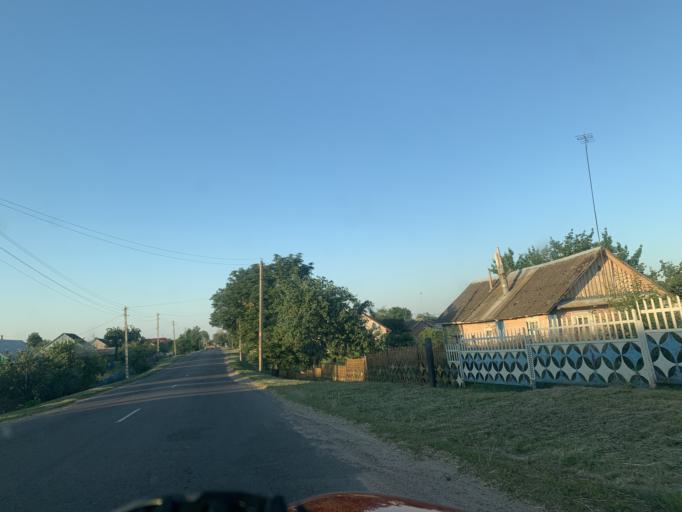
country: BY
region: Minsk
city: Haradzyeya
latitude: 53.2467
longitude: 26.5116
